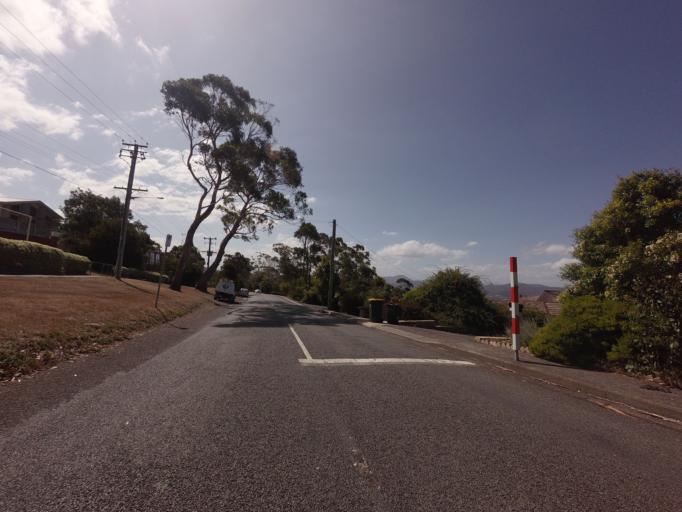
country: AU
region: Tasmania
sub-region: Hobart
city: Dynnyrne
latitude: -42.9134
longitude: 147.3237
